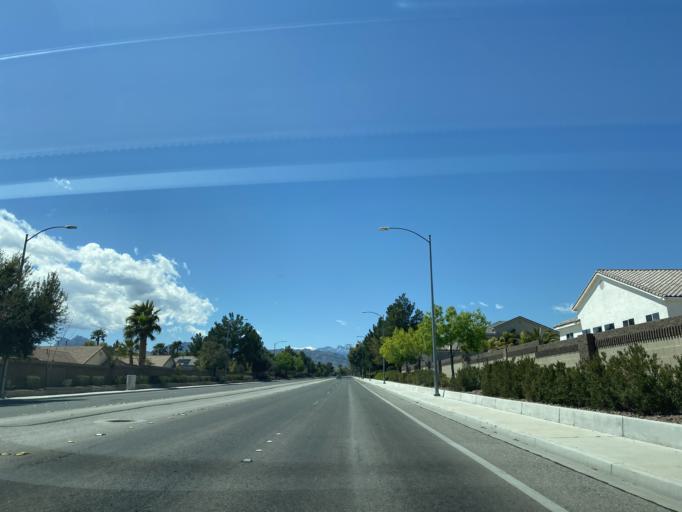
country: US
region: Nevada
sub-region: Clark County
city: North Las Vegas
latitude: 36.2979
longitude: -115.2538
